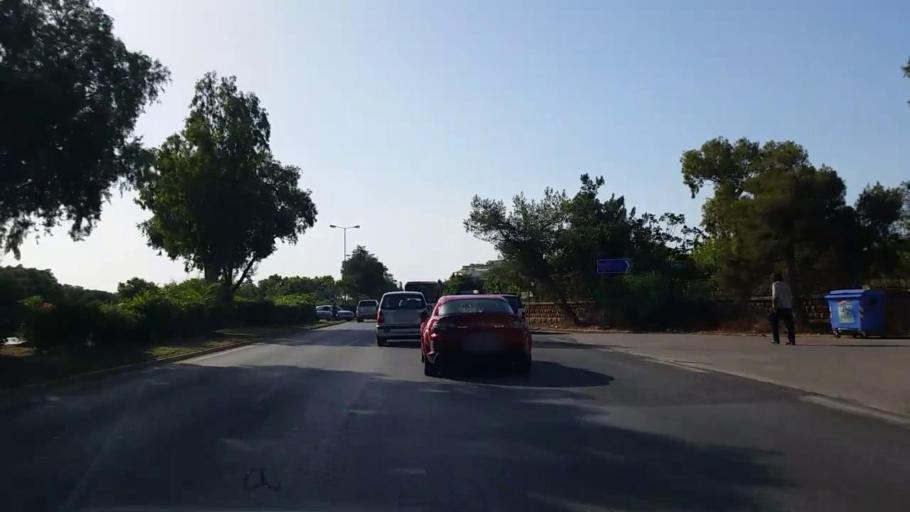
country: GR
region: Attica
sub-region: Nomarchia Anatolikis Attikis
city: Voula
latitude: 37.8419
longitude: 23.7593
